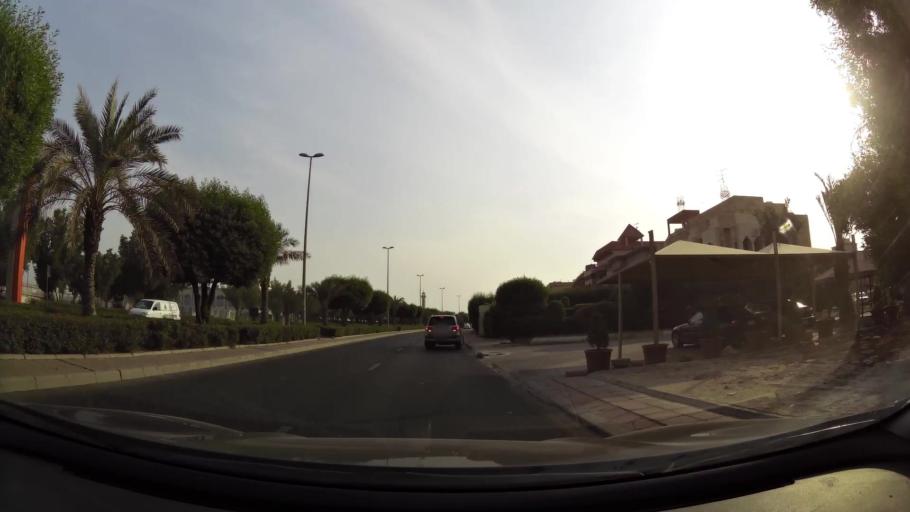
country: KW
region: Mubarak al Kabir
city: Sabah as Salim
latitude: 29.2343
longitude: 48.0622
